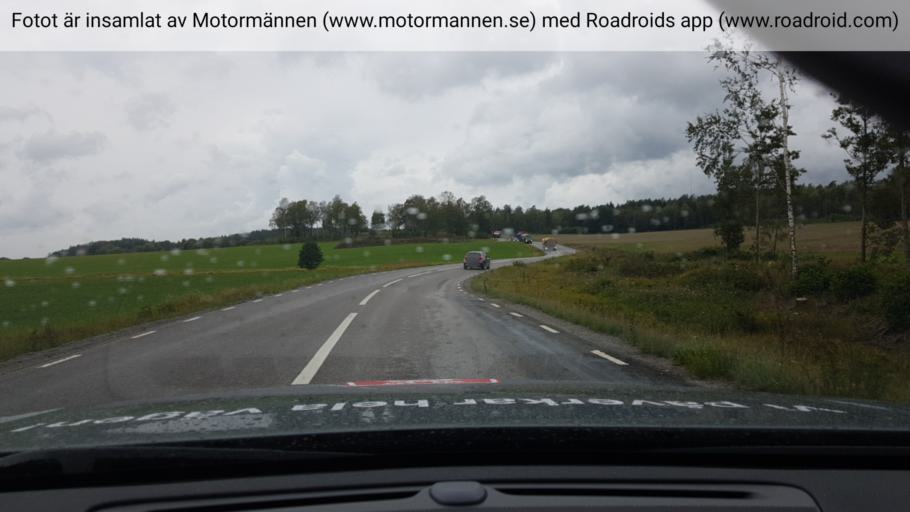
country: SE
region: Stockholm
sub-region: Botkyrka Kommun
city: Varsta
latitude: 59.1216
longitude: 17.8613
